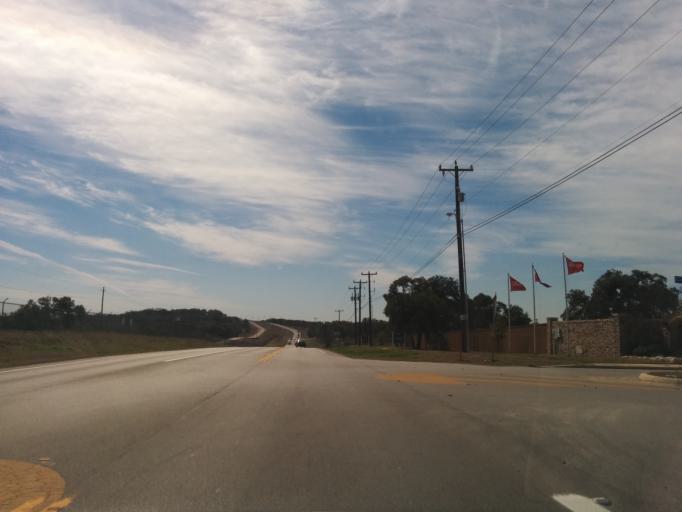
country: US
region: Texas
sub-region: Bexar County
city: Fair Oaks Ranch
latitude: 29.7061
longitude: -98.6301
